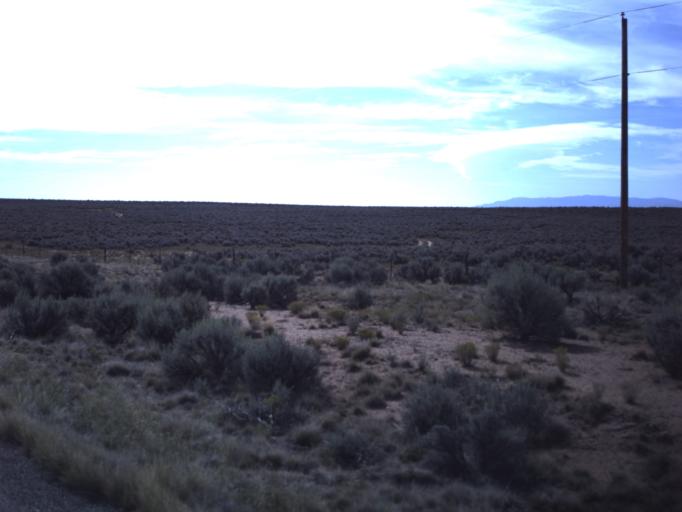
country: US
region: Utah
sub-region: San Juan County
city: Blanding
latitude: 37.4254
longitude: -109.3477
